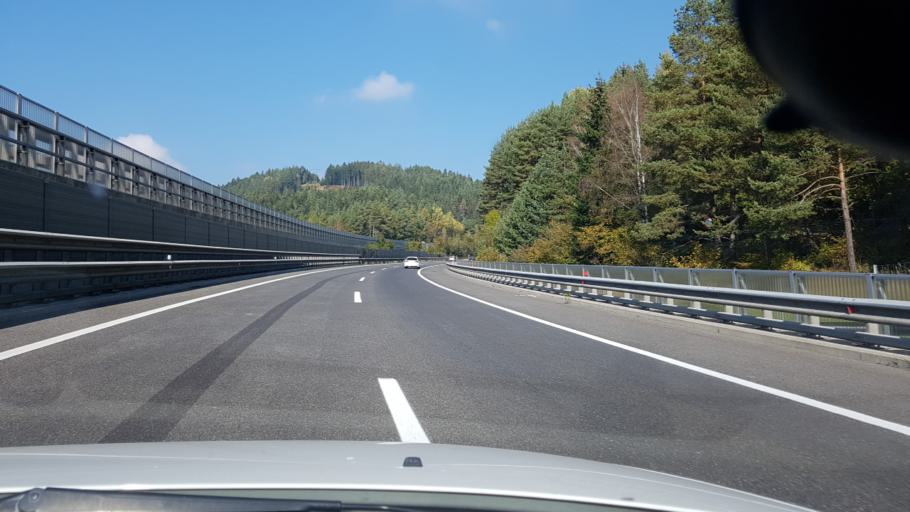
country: AT
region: Carinthia
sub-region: Politischer Bezirk Spittal an der Drau
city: Spittal an der Drau
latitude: 46.7933
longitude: 13.5185
